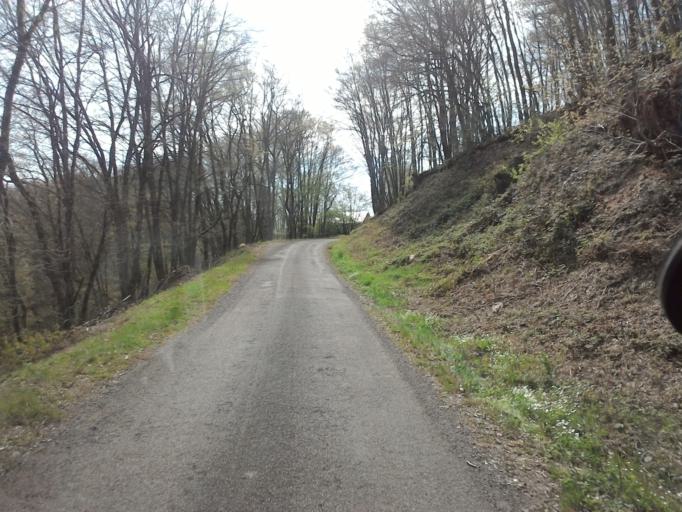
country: FR
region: Bourgogne
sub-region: Departement de la Nievre
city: Lormes
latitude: 47.3040
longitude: 3.9138
